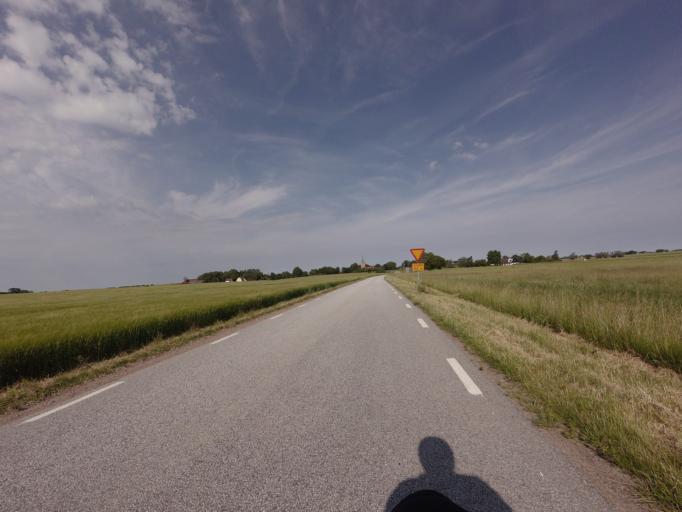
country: SE
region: Skane
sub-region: Vellinge Kommun
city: Vellinge
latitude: 55.5009
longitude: 13.0418
